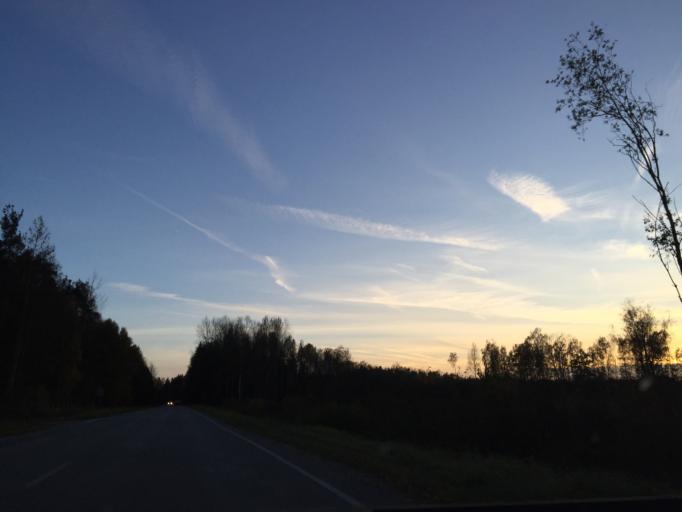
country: LV
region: Malpils
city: Malpils
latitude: 56.8850
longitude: 24.9249
